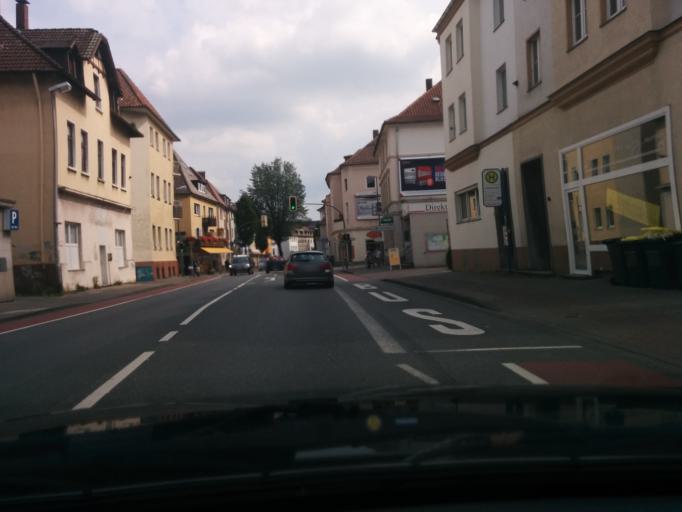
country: DE
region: North Rhine-Westphalia
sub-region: Regierungsbezirk Detmold
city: Bielefeld
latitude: 52.0271
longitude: 8.5197
